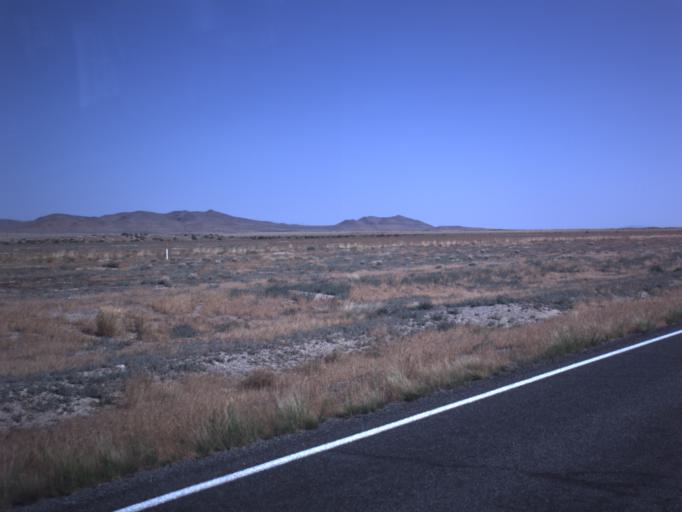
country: US
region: Utah
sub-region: Millard County
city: Delta
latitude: 38.9670
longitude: -112.8007
